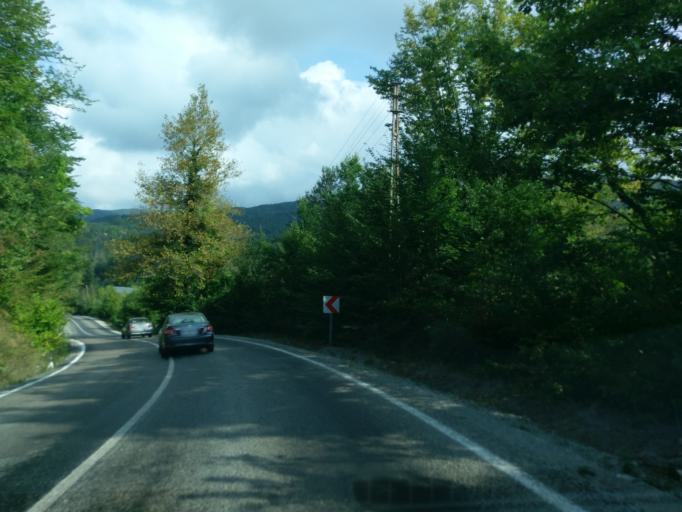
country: TR
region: Sinop
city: Ayancik
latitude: 41.8809
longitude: 34.5206
